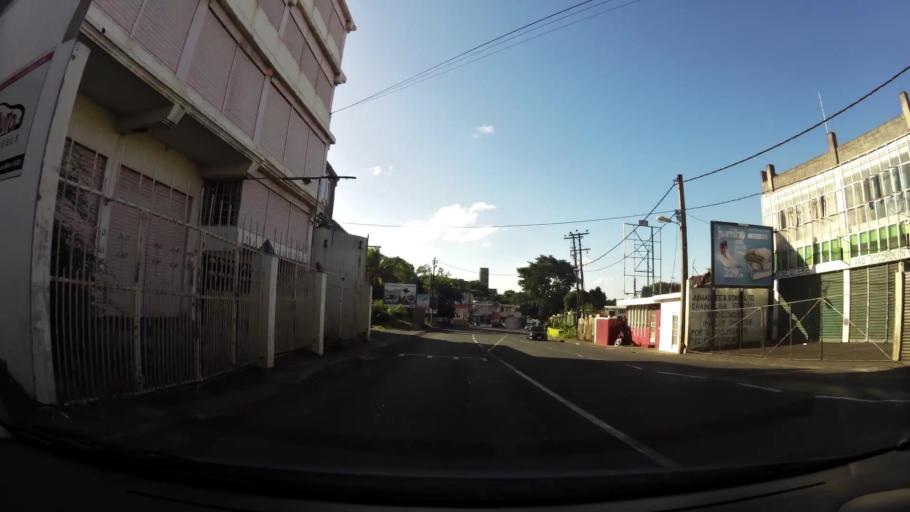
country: MU
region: Moka
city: Pailles
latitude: -20.1792
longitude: 57.4702
